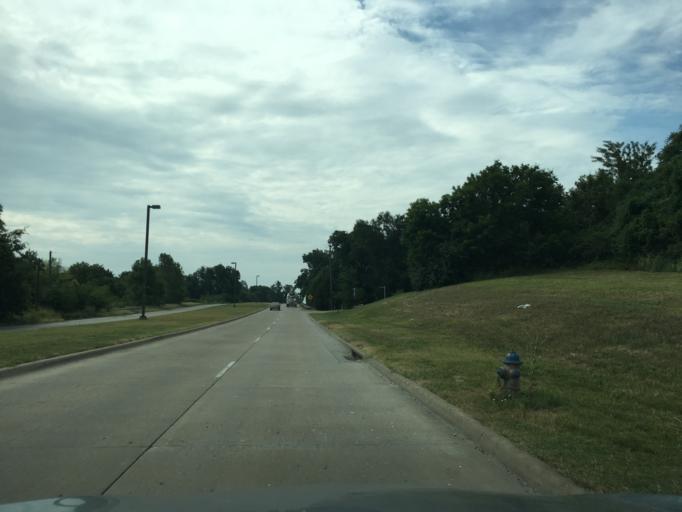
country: US
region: Texas
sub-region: Collin County
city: McKinney
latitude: 33.1970
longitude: -96.5984
